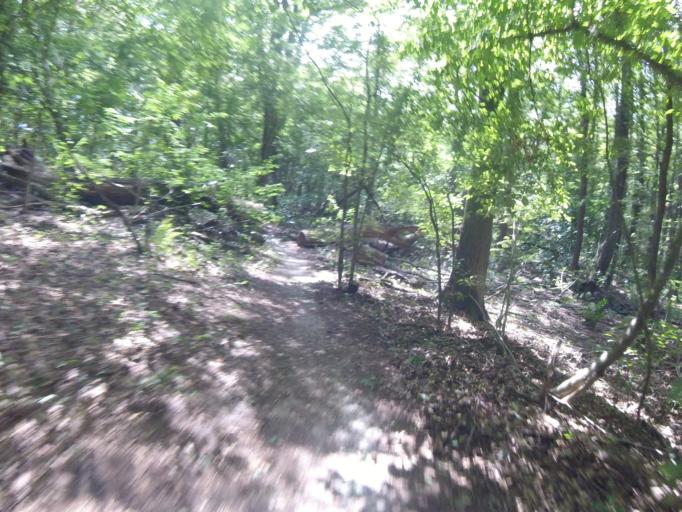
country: DE
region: Brandenburg
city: Bestensee
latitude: 52.2550
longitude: 13.6087
